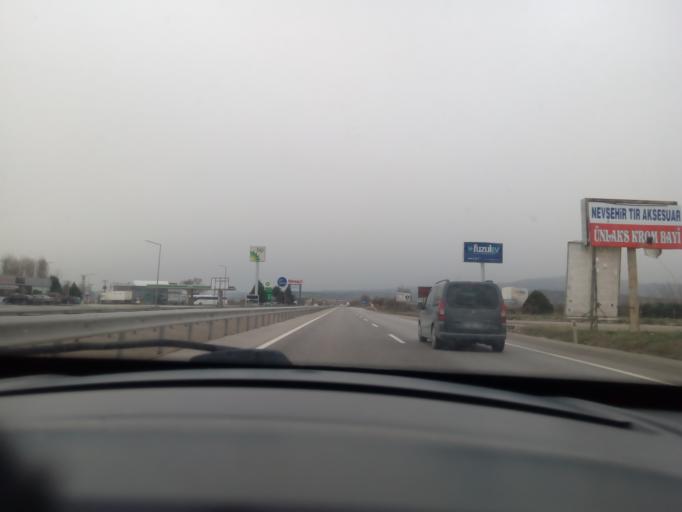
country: TR
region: Balikesir
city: Gobel
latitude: 39.9892
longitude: 28.2018
